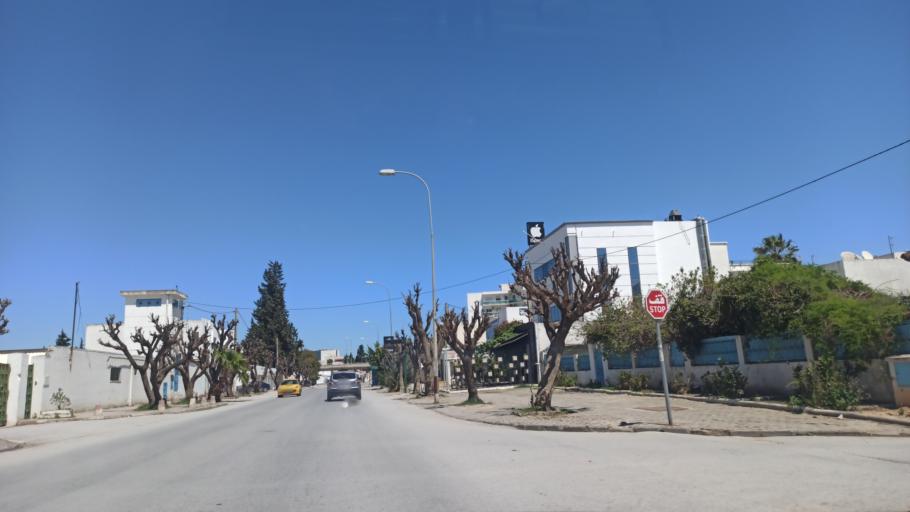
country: TN
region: Tunis
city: Tunis
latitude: 36.8289
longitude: 10.1855
